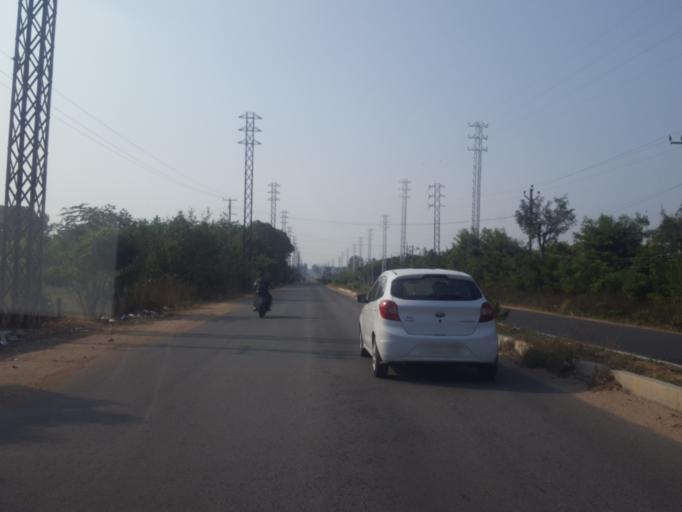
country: IN
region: Telangana
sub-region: Medak
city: Serilingampalle
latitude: 17.4005
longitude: 78.2955
